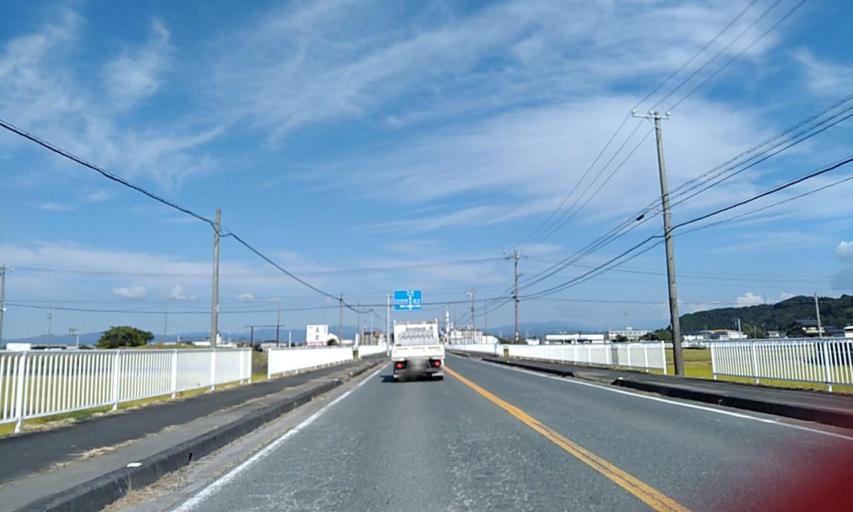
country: JP
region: Shizuoka
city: Hamakita
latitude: 34.7615
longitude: 137.8302
